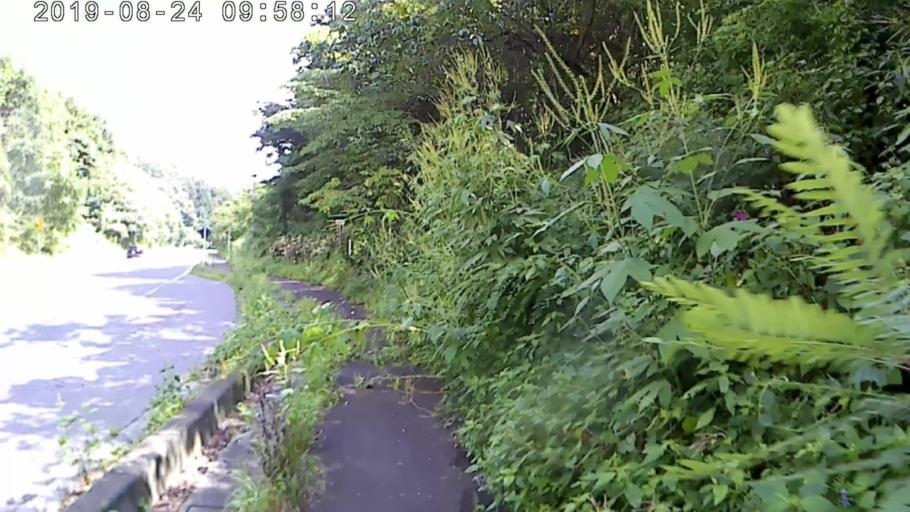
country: JP
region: Nagano
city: Kamimaruko
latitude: 36.2583
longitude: 138.2878
